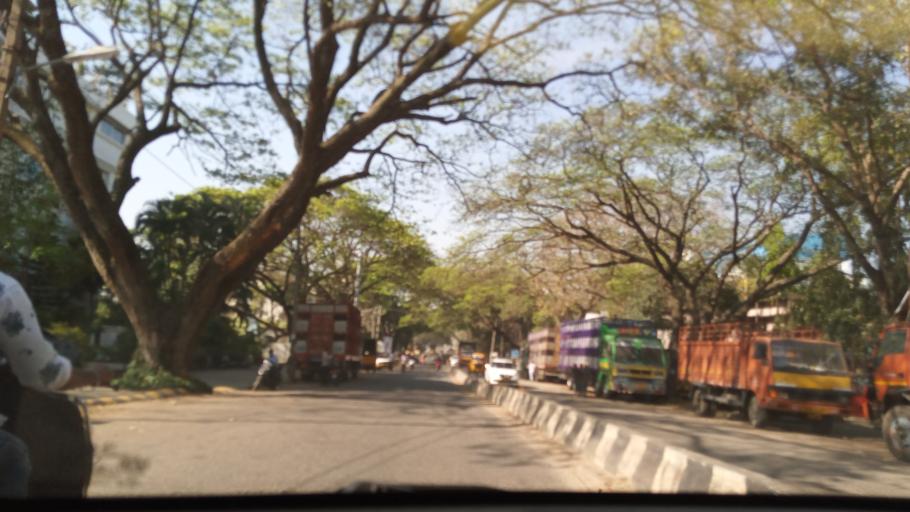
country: IN
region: Karnataka
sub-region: Bangalore Urban
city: Bangalore
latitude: 13.0219
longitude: 77.5415
